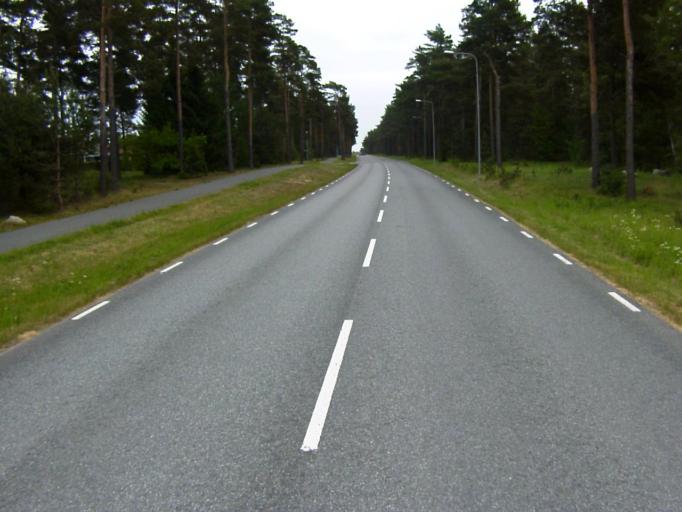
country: SE
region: Skane
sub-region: Kristianstads Kommun
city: Ahus
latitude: 55.9357
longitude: 14.2707
